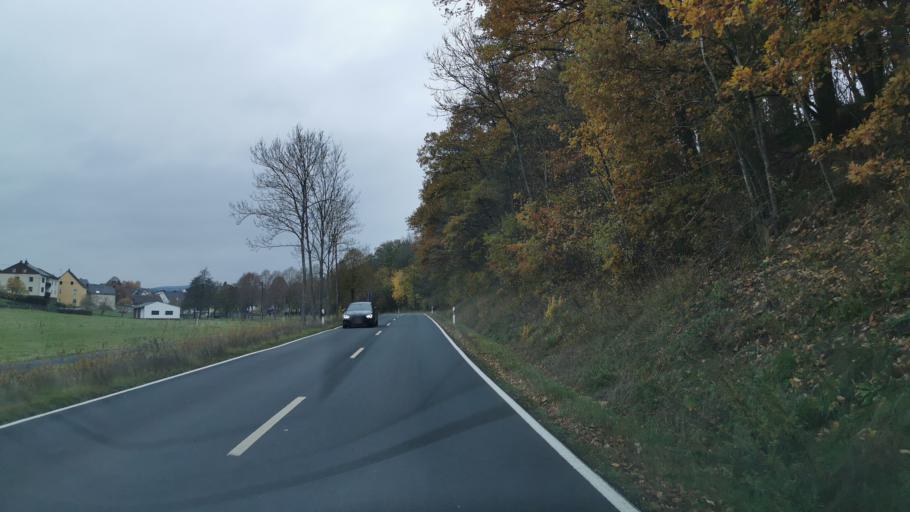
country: DE
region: Rheinland-Pfalz
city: Schonbach
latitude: 50.2130
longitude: 6.9514
